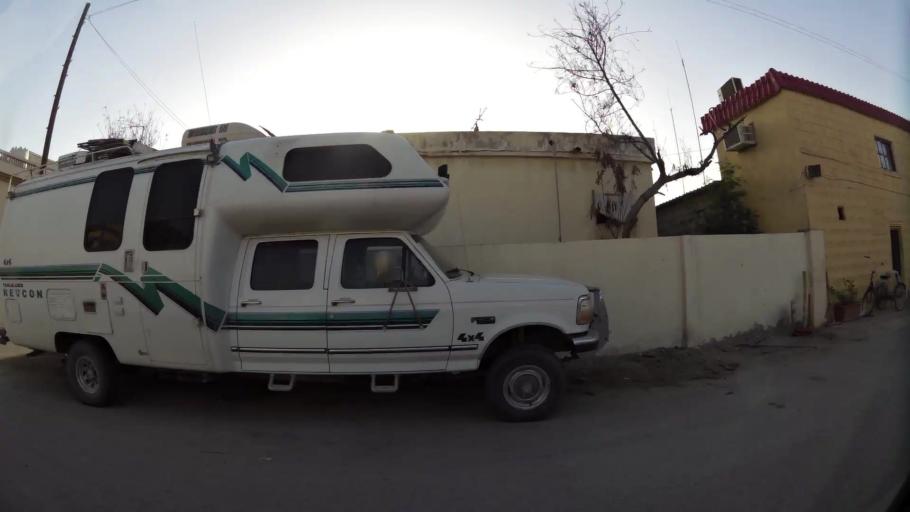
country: QA
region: Baladiyat ar Rayyan
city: Ar Rayyan
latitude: 25.3239
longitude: 51.4581
